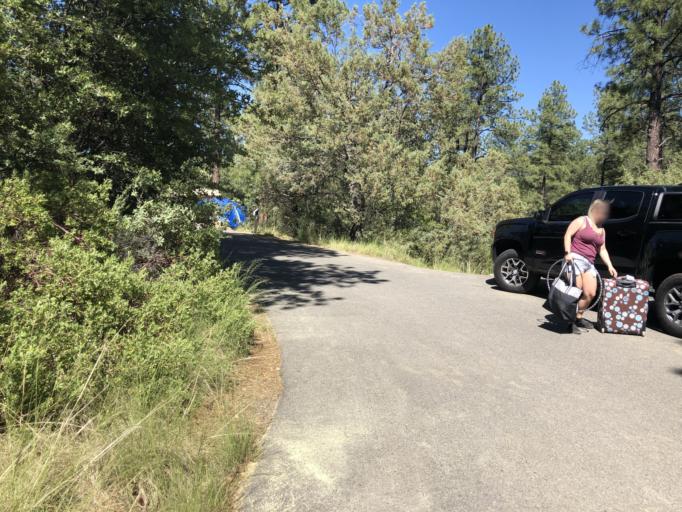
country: US
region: Arizona
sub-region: Yavapai County
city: Prescott
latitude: 34.5155
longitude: -112.3879
